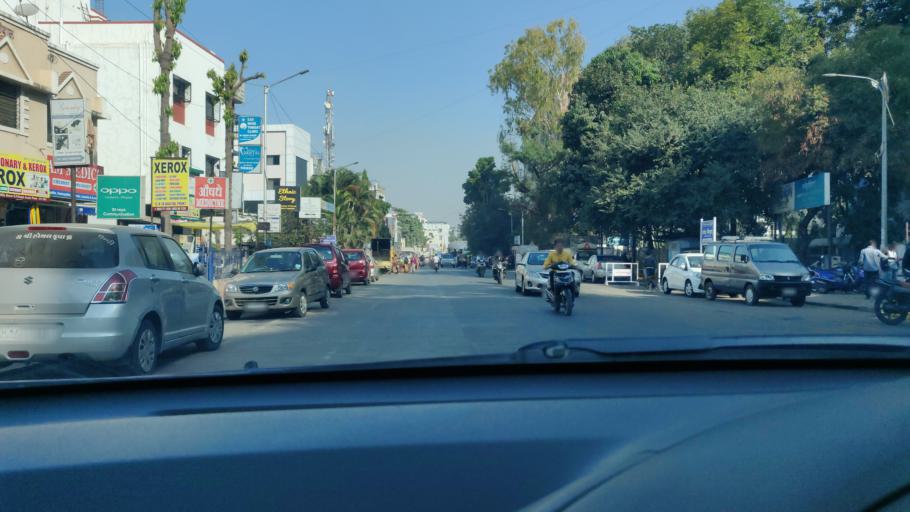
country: IN
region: Maharashtra
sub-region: Pune Division
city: Khadki
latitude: 18.5590
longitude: 73.8035
